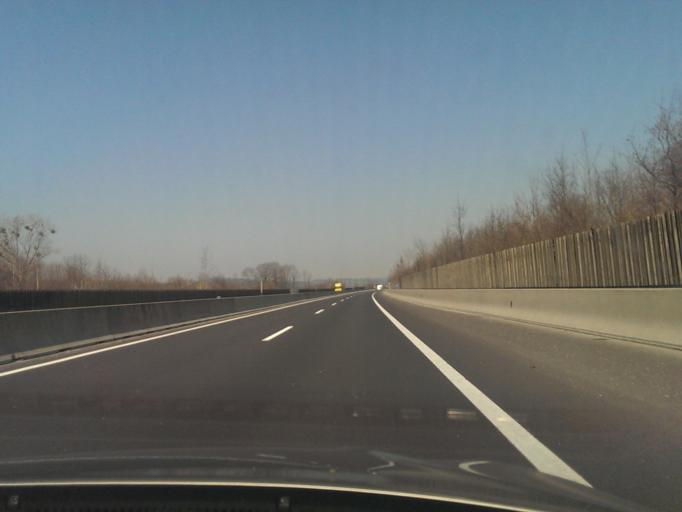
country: AT
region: Upper Austria
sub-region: Politischer Bezirk Kirchdorf an der Krems
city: Micheldorf in Oberoesterreich
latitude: 47.8981
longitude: 14.1032
